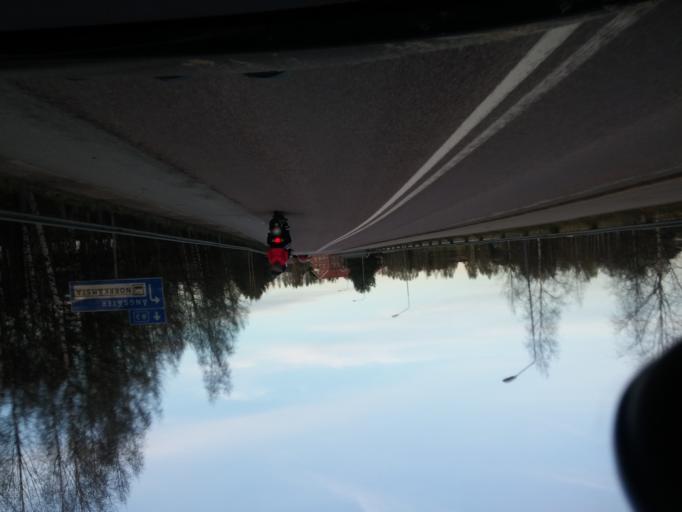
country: SE
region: Gaevleborg
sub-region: Ljusdals Kommun
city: Ljusdal
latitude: 61.8348
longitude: 16.0670
